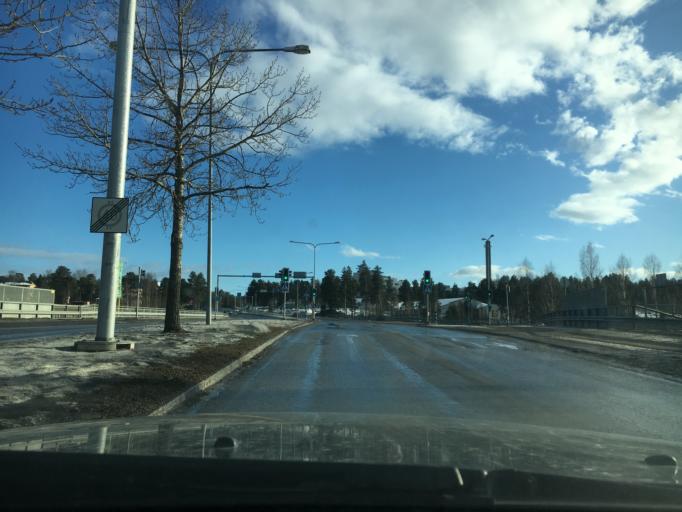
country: FI
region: Kainuu
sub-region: Kajaani
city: Kajaani
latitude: 64.2196
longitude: 27.7292
